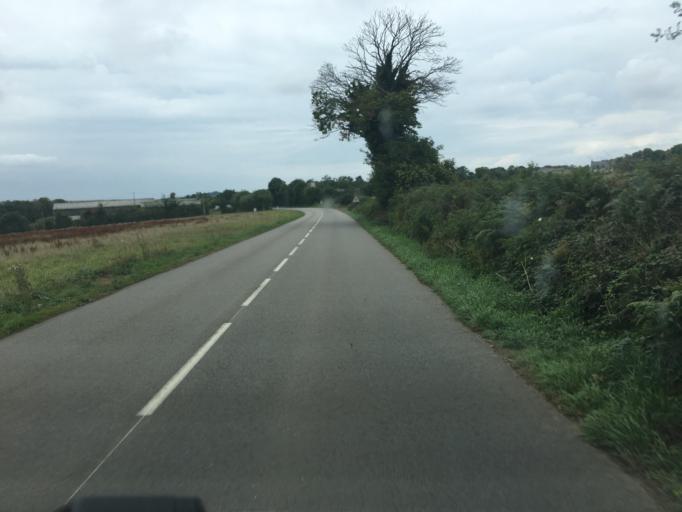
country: FR
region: Brittany
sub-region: Departement du Finistere
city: Plonevez-Porzay
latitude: 48.1280
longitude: -4.2285
